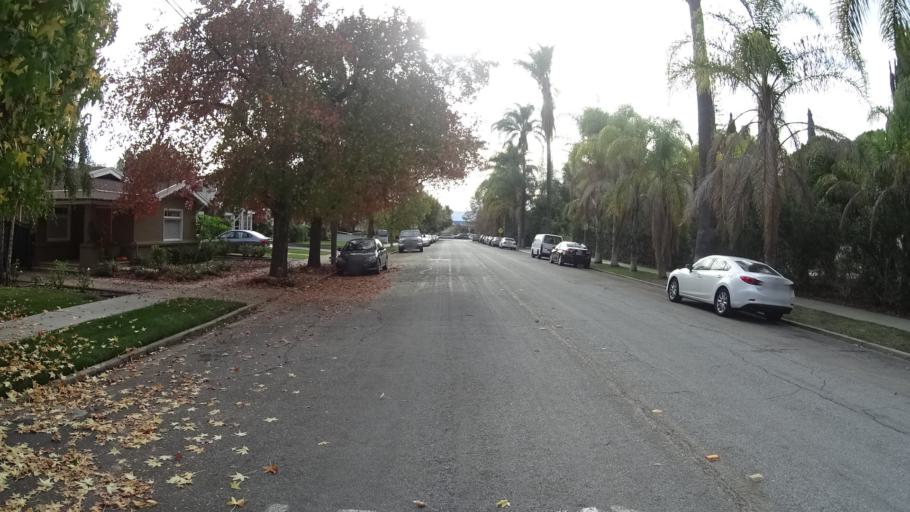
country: US
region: California
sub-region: Santa Clara County
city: Buena Vista
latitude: 37.3337
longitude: -121.9214
